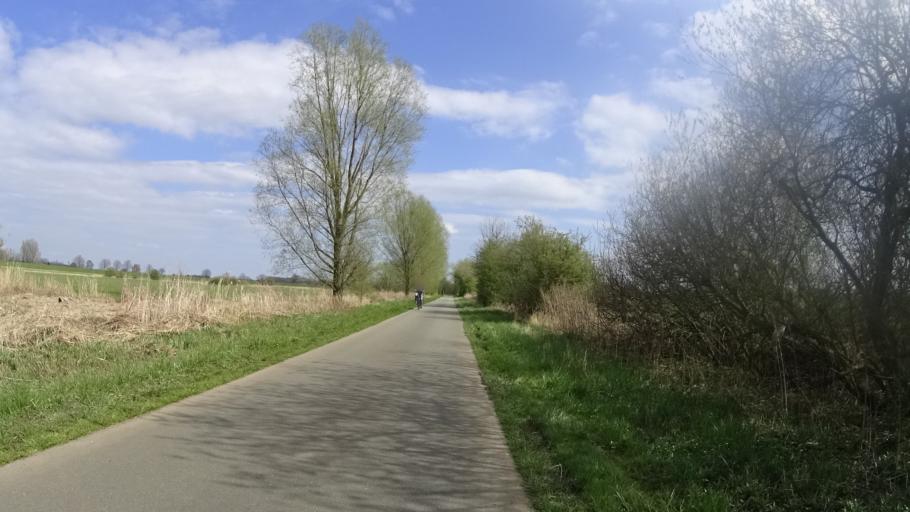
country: DE
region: Lower Saxony
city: Rhede
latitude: 53.0562
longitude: 7.3003
